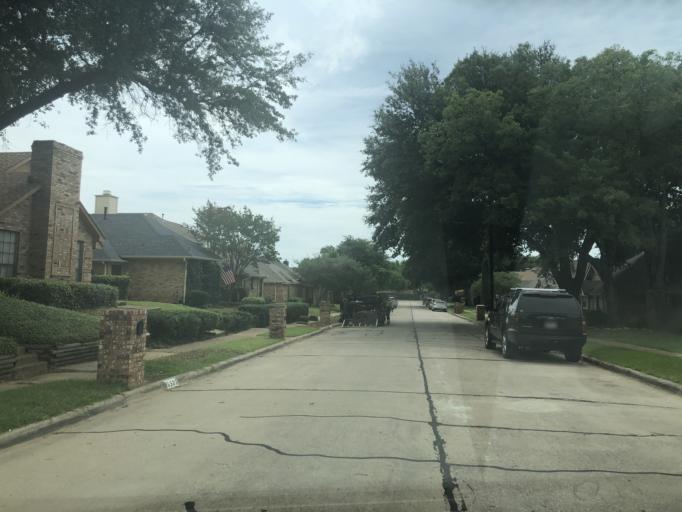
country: US
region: Texas
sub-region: Dallas County
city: Irving
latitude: 32.7933
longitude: -96.9792
